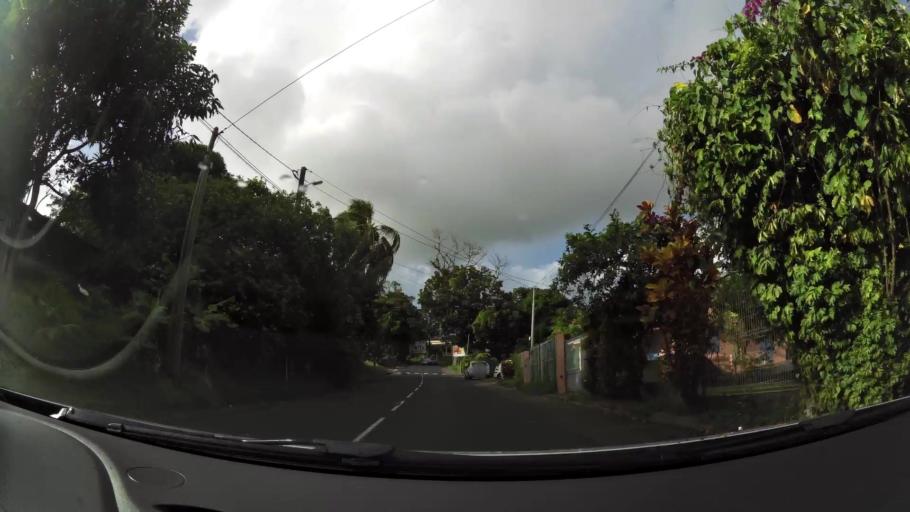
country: MQ
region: Martinique
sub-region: Martinique
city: Ducos
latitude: 14.5715
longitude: -60.9648
